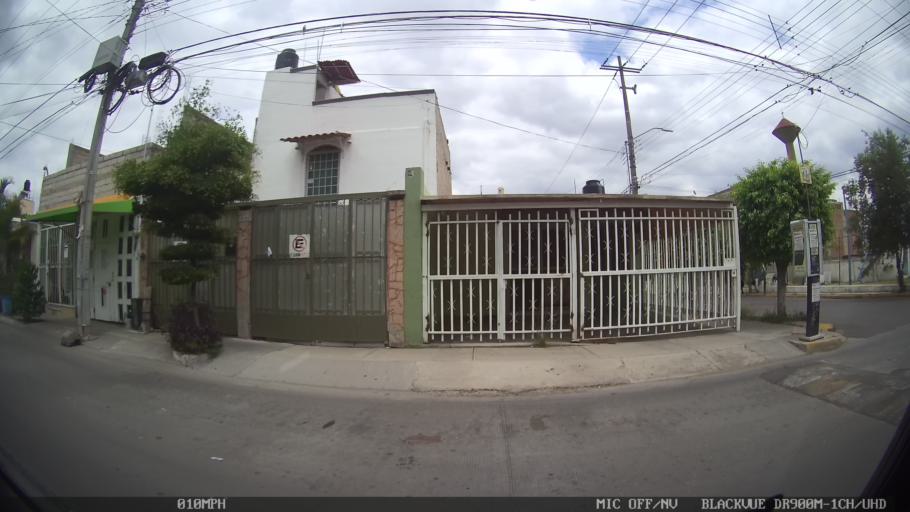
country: MX
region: Jalisco
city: Tonala
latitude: 20.6390
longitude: -103.2525
